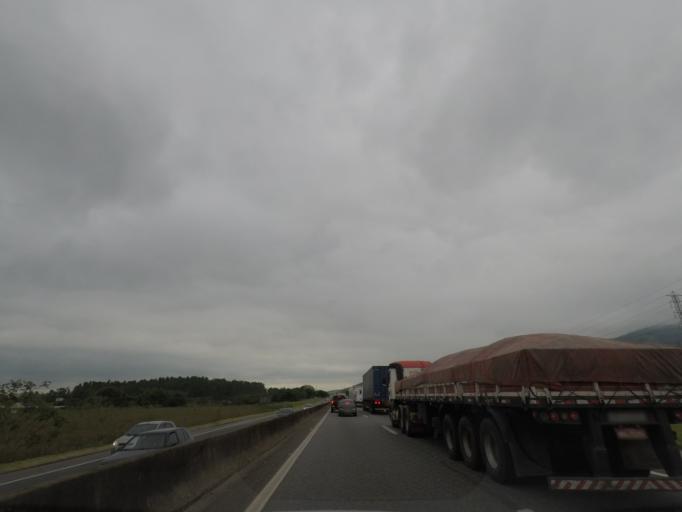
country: BR
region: Sao Paulo
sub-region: Aparecida
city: Aparecida
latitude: -22.8954
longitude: -45.2965
